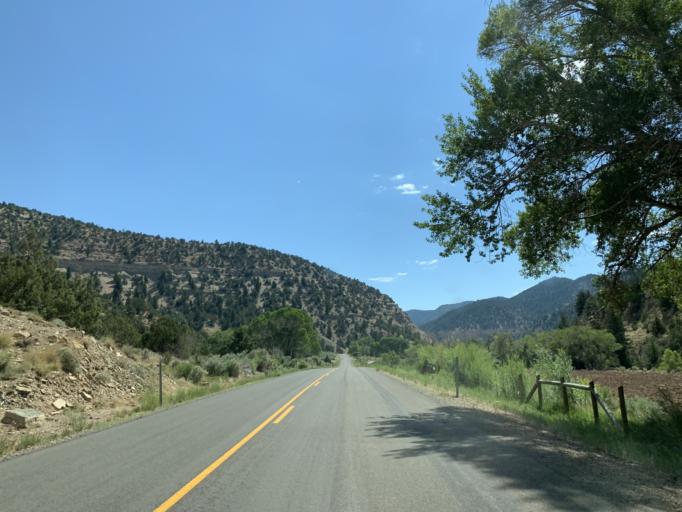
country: US
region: Utah
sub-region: Carbon County
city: East Carbon City
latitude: 39.7764
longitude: -110.4726
